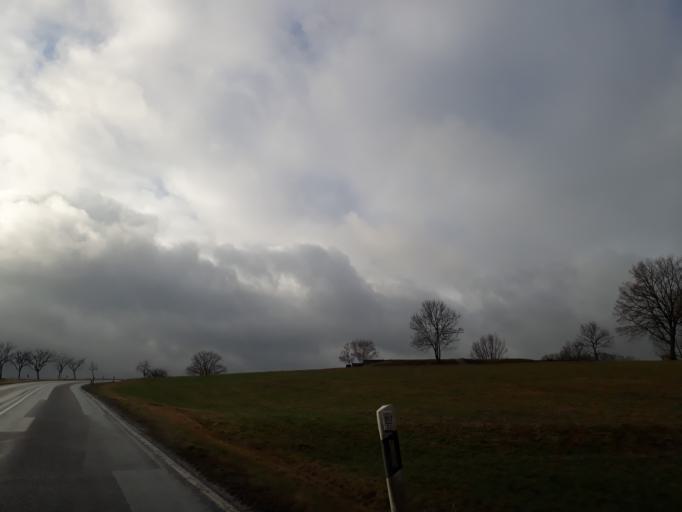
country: DE
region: Saxony
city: Herrnhut
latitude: 50.9960
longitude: 14.7209
